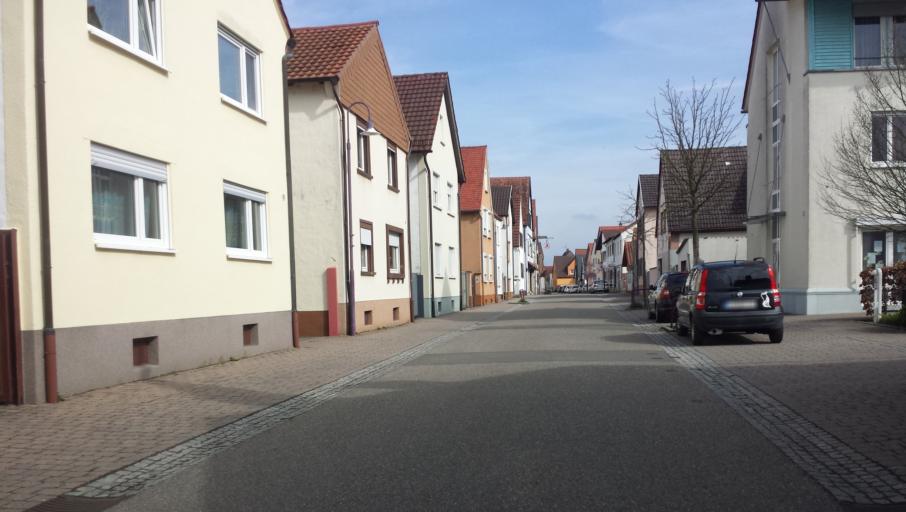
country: DE
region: Rheinland-Pfalz
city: Dudenhofen
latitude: 49.2655
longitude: 8.4003
